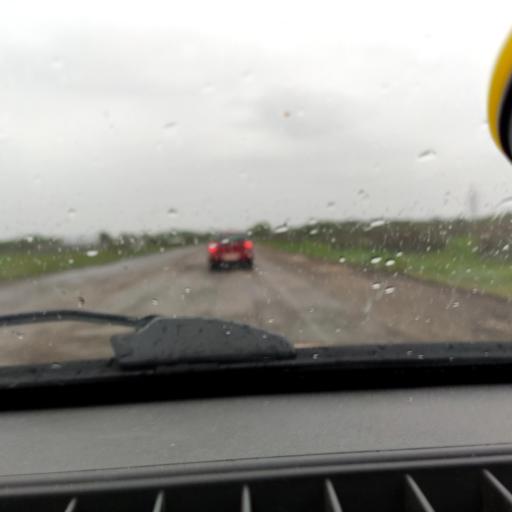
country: RU
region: Samara
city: Tol'yatti
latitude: 53.6671
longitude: 49.4182
